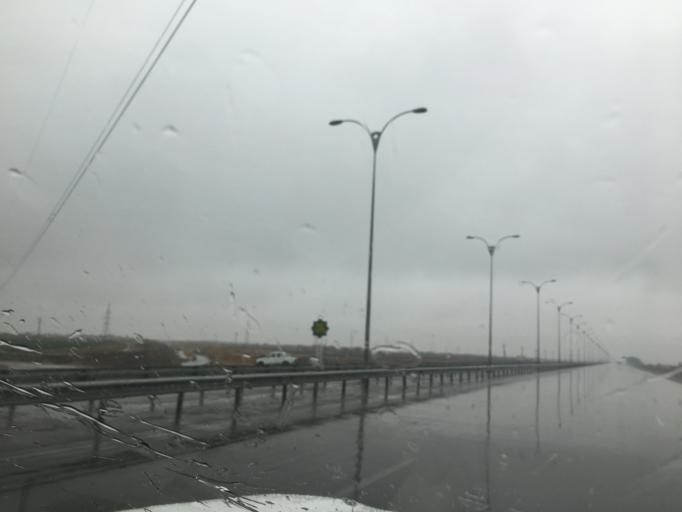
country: TM
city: Murgab
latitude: 37.5239
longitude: 61.9098
